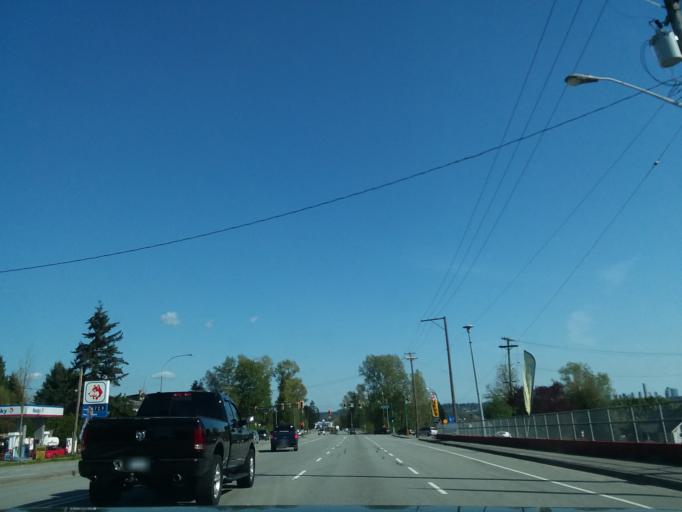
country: CA
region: British Columbia
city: New Westminster
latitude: 49.2404
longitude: -122.8829
